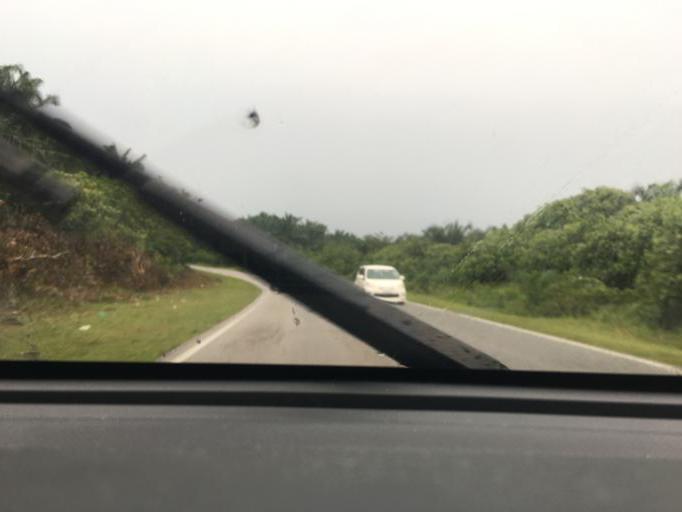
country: MY
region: Kedah
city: Sungai Petani
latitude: 5.6391
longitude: 100.6283
